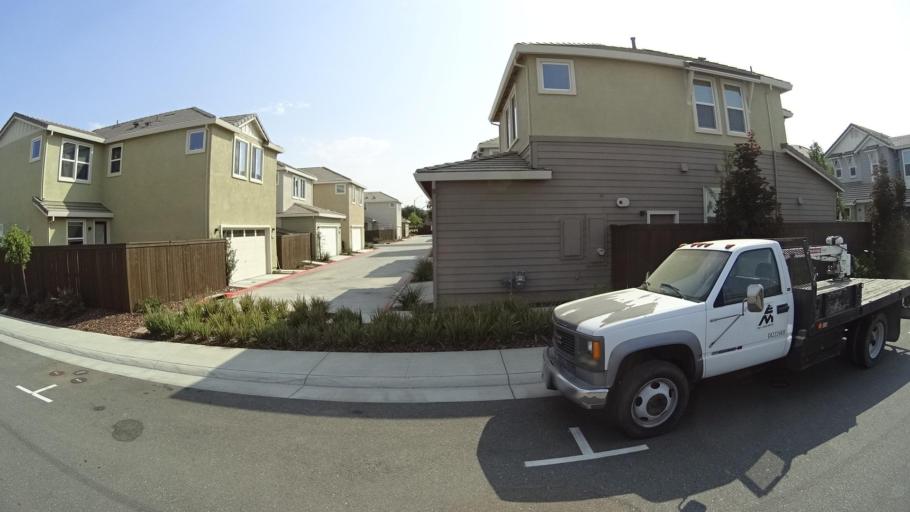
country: US
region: California
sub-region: Placer County
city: Rocklin
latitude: 38.8016
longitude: -121.2117
